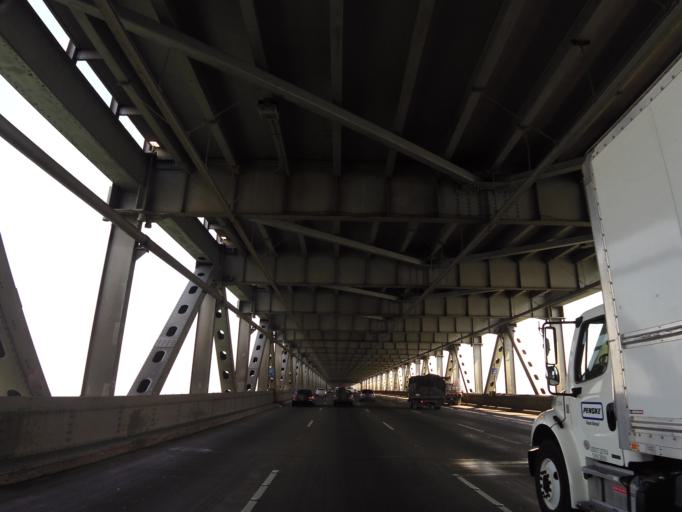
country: US
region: California
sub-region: San Francisco County
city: San Francisco
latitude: 37.7934
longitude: -122.3838
